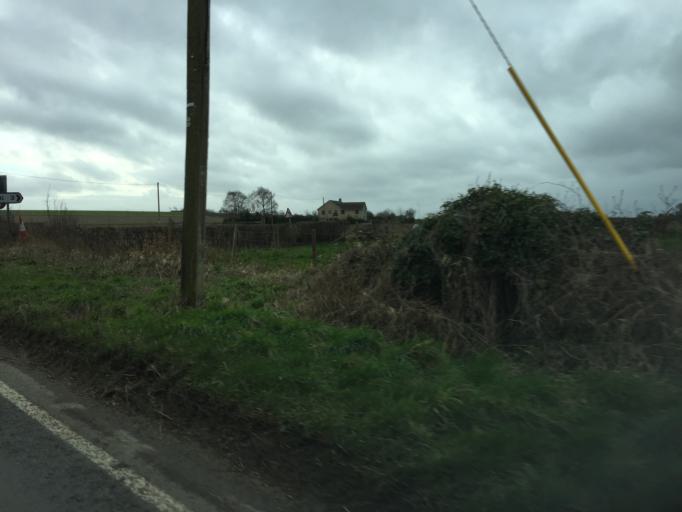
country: GB
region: England
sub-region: Gloucestershire
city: Lechlade
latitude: 51.6794
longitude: -1.6757
